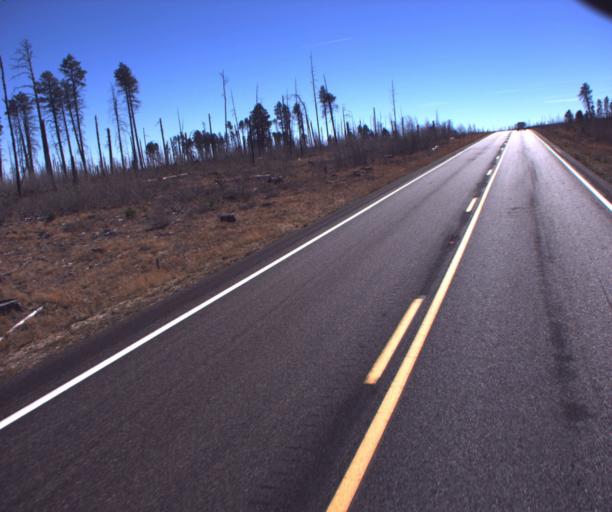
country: US
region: Arizona
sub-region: Coconino County
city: Fredonia
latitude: 36.6018
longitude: -112.1809
